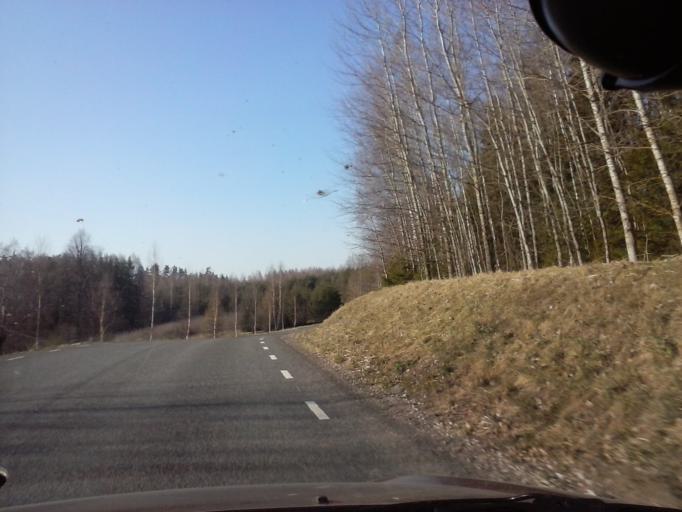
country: EE
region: Tartu
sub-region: UElenurme vald
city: Ulenurme
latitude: 58.1620
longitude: 26.8484
